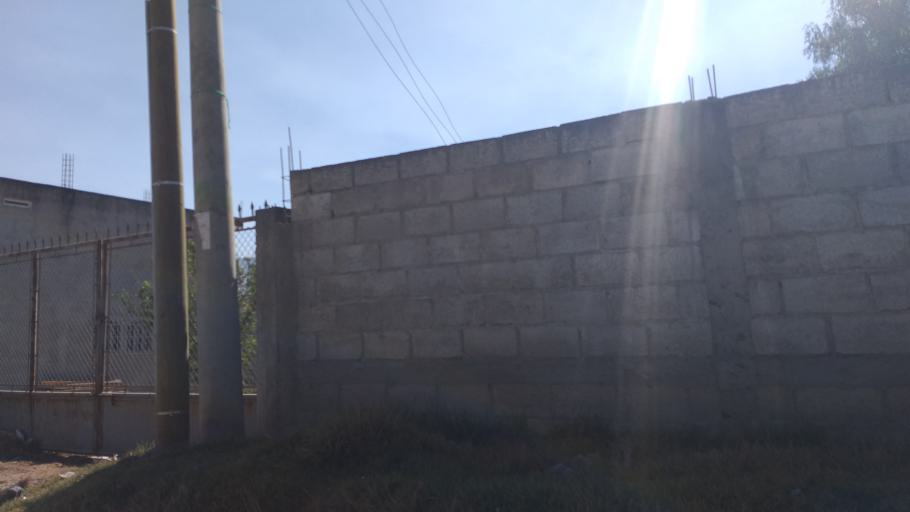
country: GT
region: Quetzaltenango
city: Quetzaltenango
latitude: 14.7986
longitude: -91.5436
